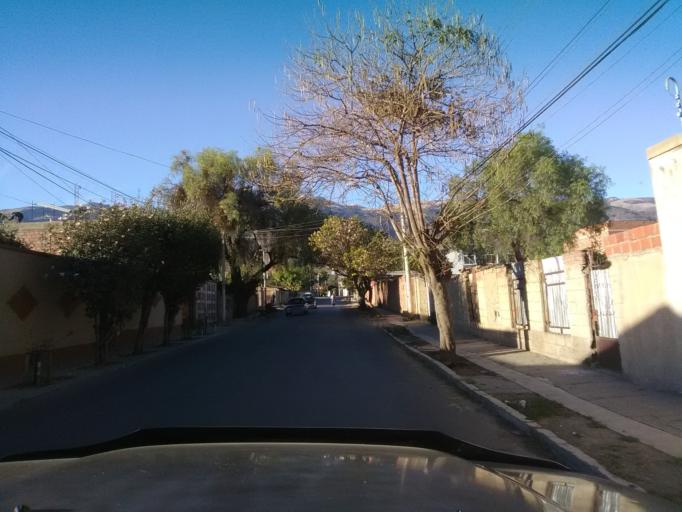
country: BO
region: Cochabamba
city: Cochabamba
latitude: -17.3644
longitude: -66.1866
